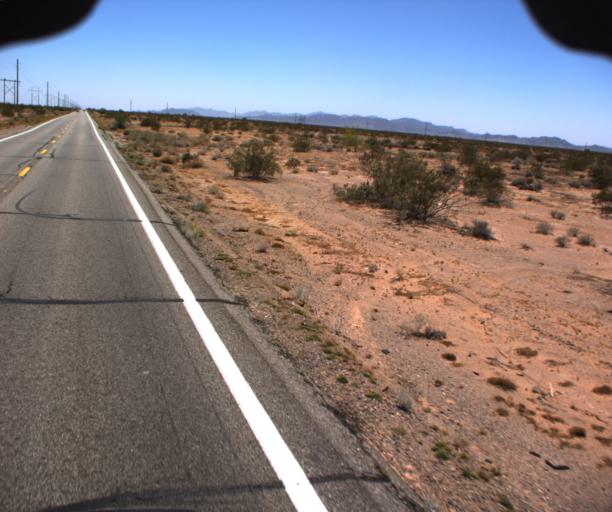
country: US
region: Arizona
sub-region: La Paz County
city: Quartzsite
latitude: 33.8567
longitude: -114.2170
